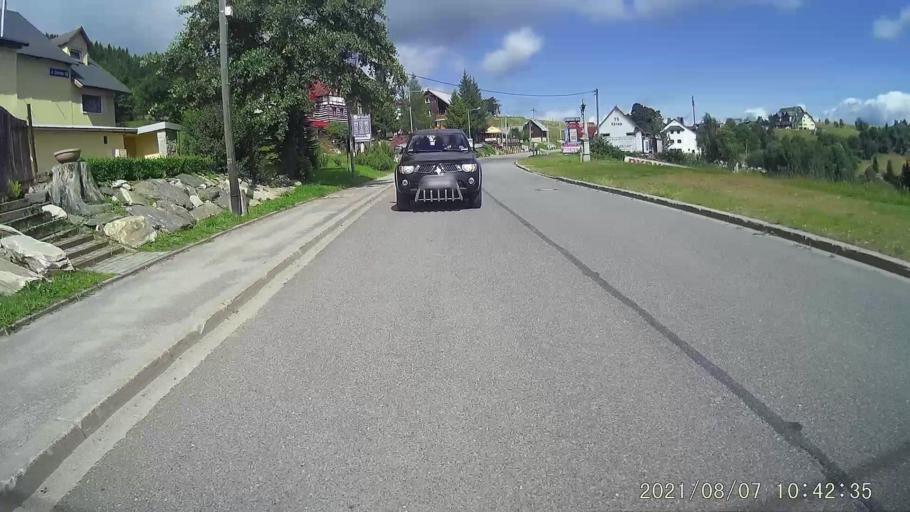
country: PL
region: Lower Silesian Voivodeship
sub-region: Powiat klodzki
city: Duszniki-Zdroj
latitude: 50.3307
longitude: 16.3902
